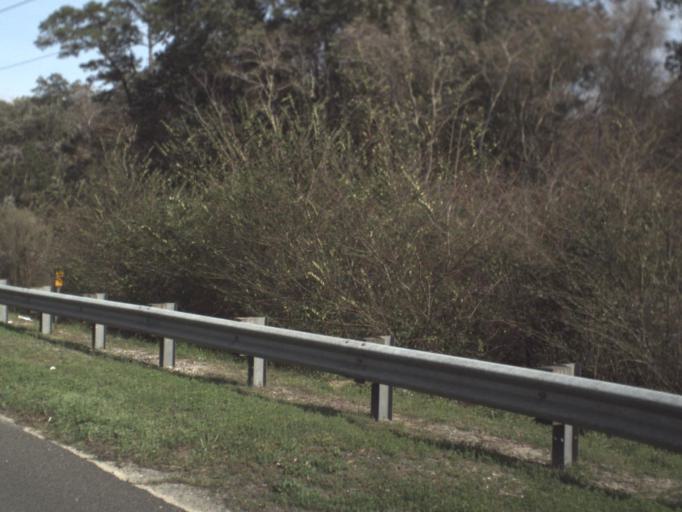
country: US
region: Florida
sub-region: Bay County
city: Hiland Park
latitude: 30.2062
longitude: -85.6172
